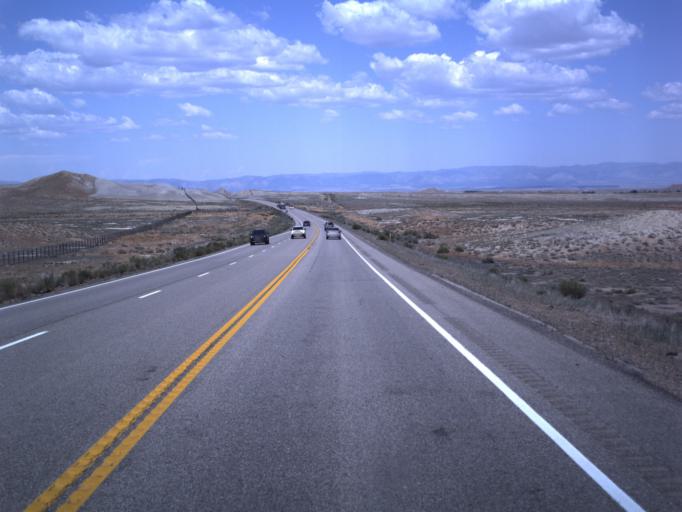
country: US
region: Utah
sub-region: Emery County
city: Huntington
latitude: 39.4085
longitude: -110.8827
